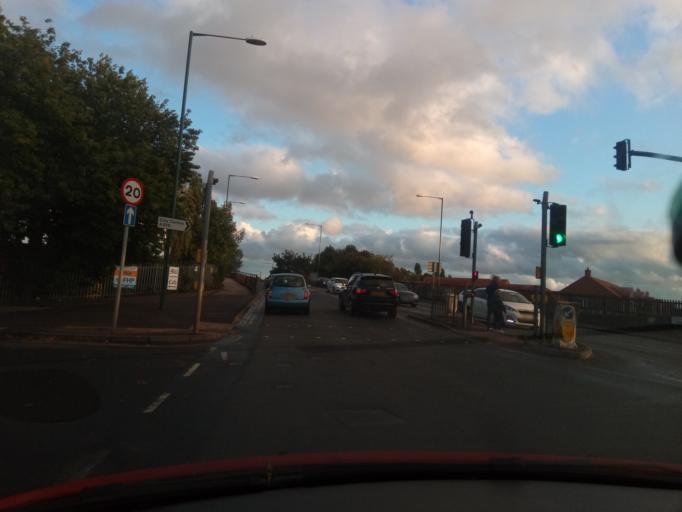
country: GB
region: England
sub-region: Nottingham
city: Nottingham
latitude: 52.9675
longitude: -1.1838
